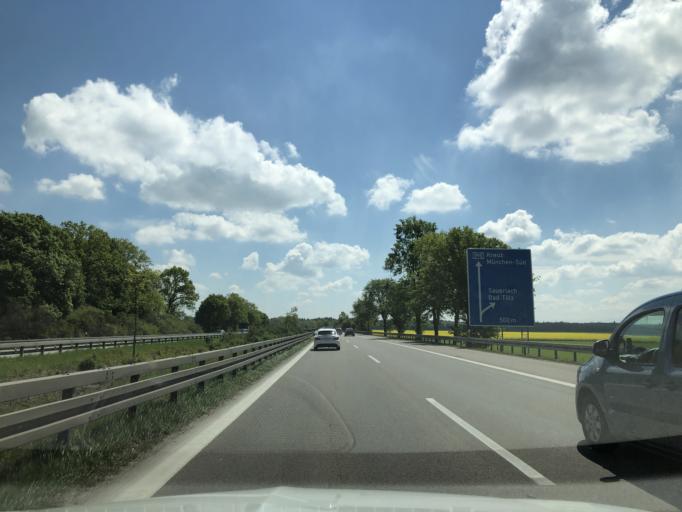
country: DE
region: Bavaria
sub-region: Upper Bavaria
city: Taufkirchen
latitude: 48.0303
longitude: 11.6184
